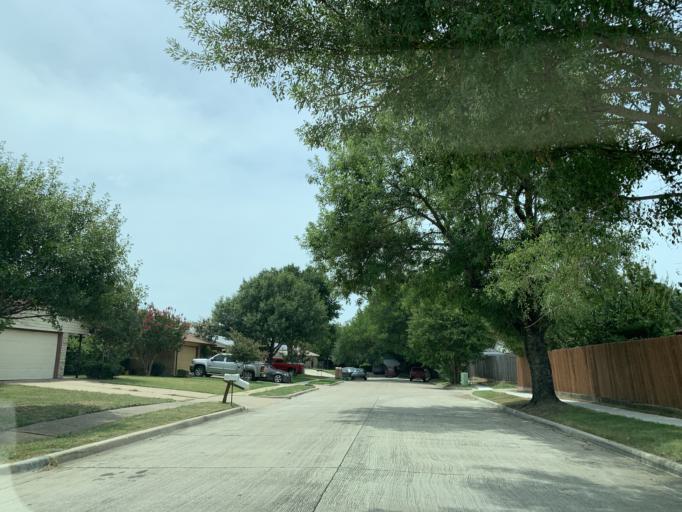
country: US
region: Texas
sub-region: Dallas County
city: Cedar Hill
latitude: 32.6541
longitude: -97.0178
